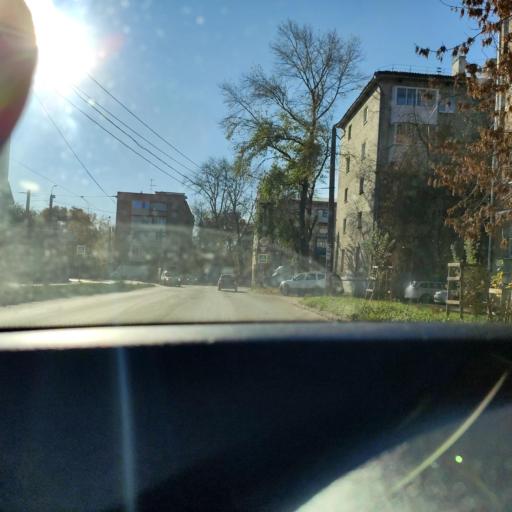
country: RU
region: Samara
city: Samara
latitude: 53.2025
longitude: 50.2316
